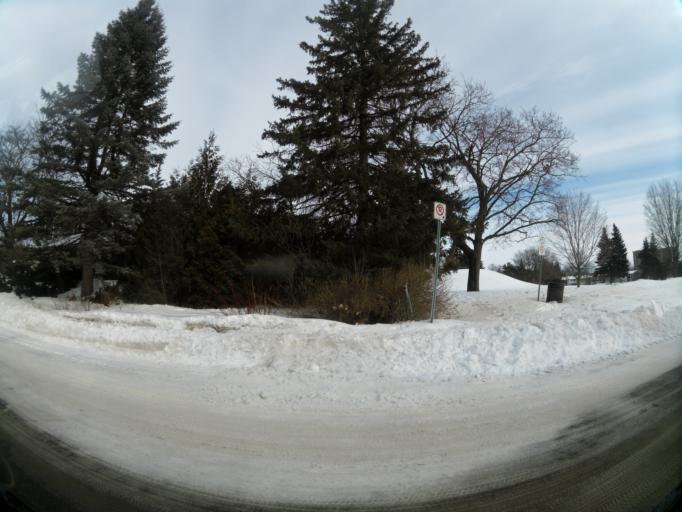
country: CA
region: Ontario
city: Ottawa
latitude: 45.4408
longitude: -75.6002
